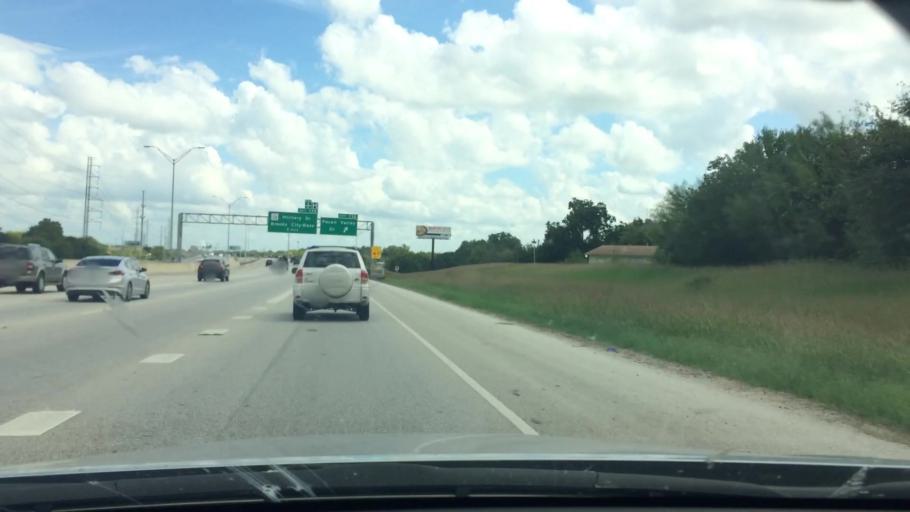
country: US
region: Texas
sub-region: Bexar County
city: San Antonio
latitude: 29.3643
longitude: -98.4464
